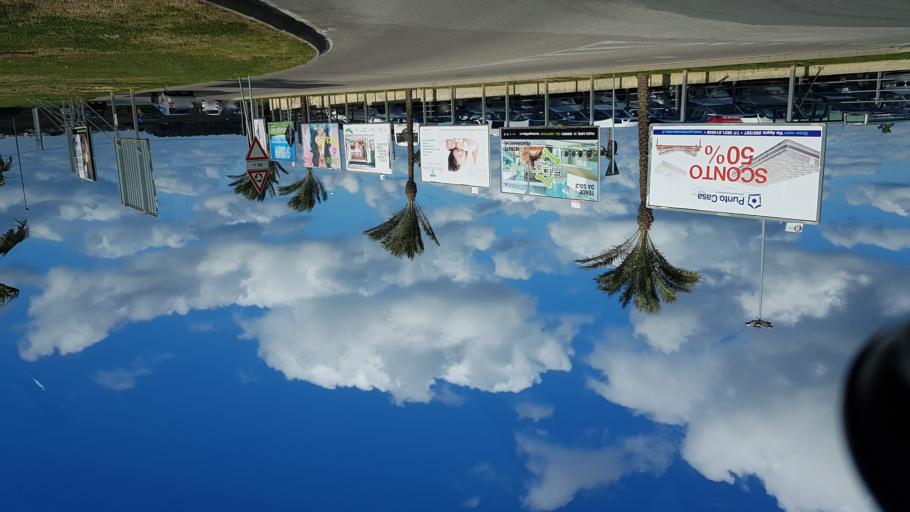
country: IT
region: Apulia
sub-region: Provincia di Brindisi
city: Brindisi
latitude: 40.6187
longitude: 17.9038
